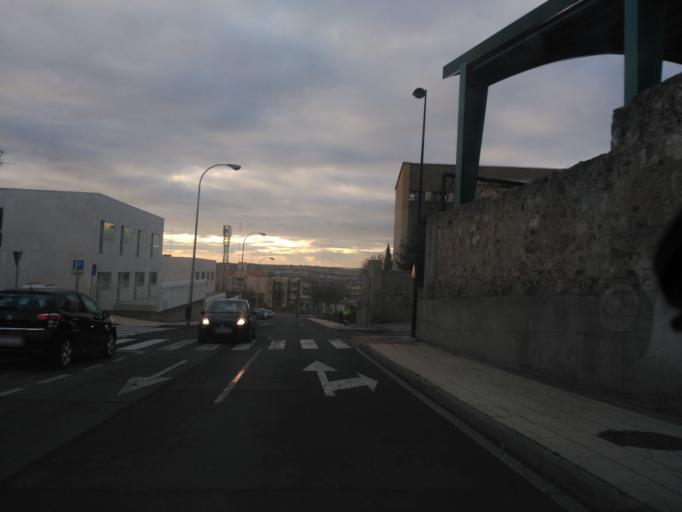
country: ES
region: Castille and Leon
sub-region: Provincia de Salamanca
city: Salamanca
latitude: 40.9654
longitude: -5.6490
